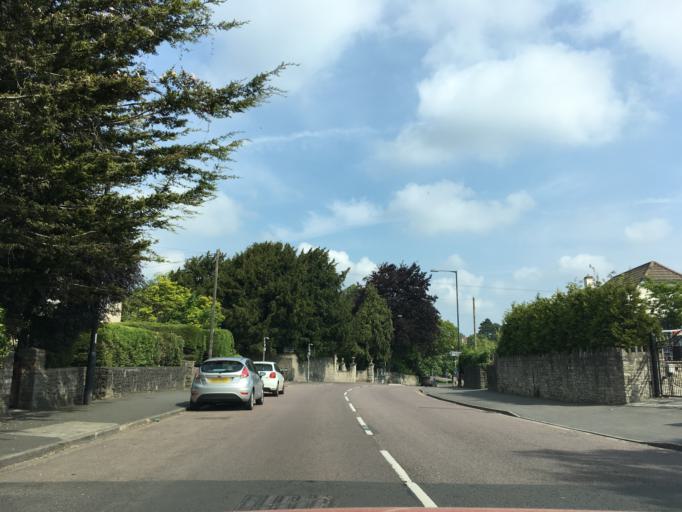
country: GB
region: England
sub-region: North Somerset
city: Dundry
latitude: 51.4169
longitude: -2.6176
